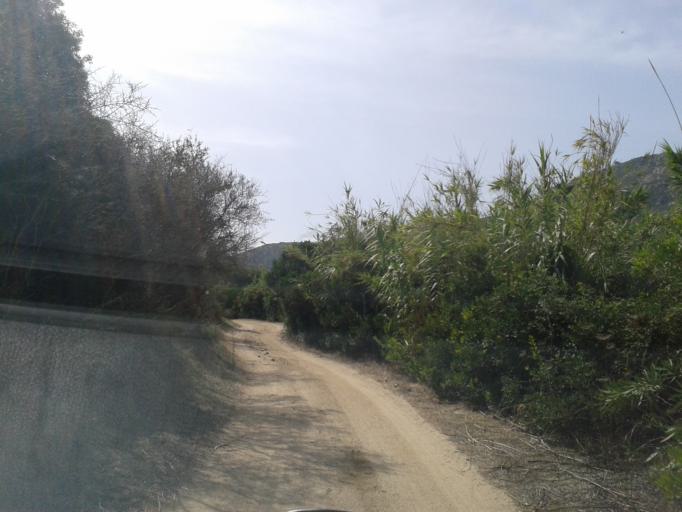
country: IT
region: Sardinia
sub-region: Provincia di Cagliari
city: Villasimius
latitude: 39.1374
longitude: 9.4903
